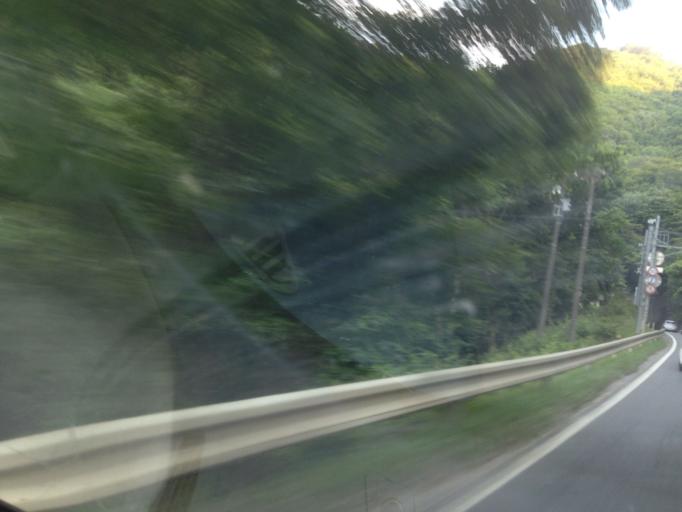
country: JP
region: Iwate
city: Kamaishi
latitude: 39.2935
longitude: 141.8826
